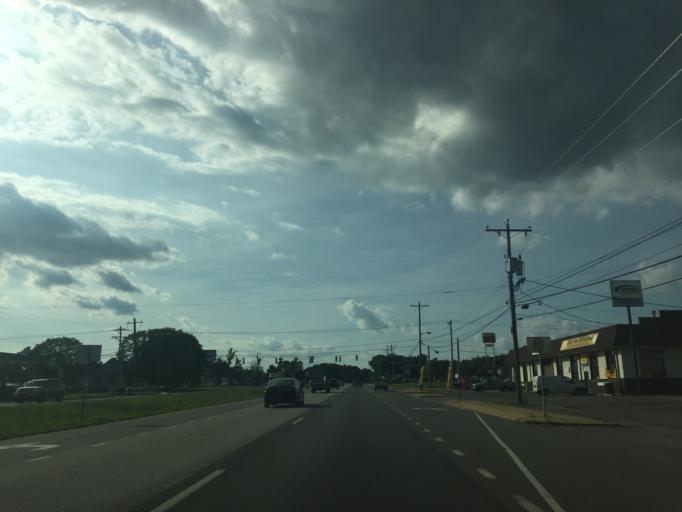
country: US
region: Delaware
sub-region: Kent County
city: Smyrna
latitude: 39.3147
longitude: -75.6142
